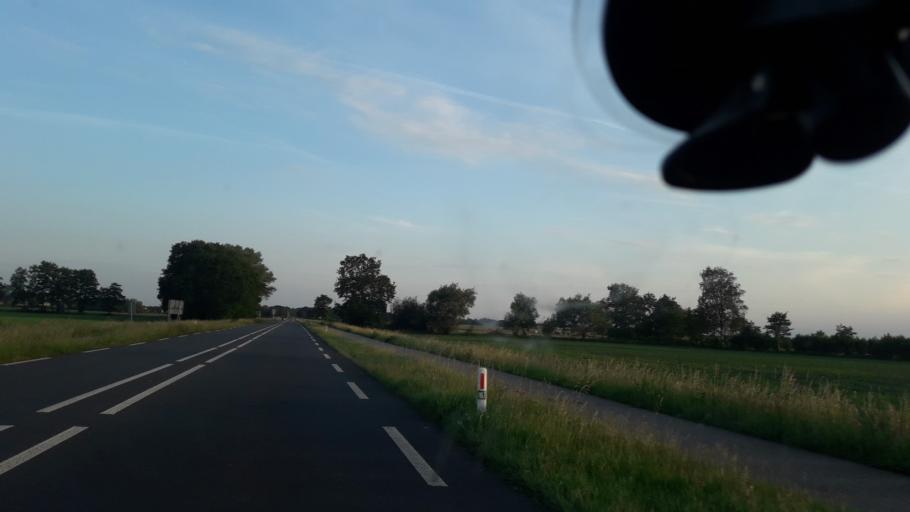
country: NL
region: Gelderland
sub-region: Gemeente Elburg
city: Elburg
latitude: 52.4379
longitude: 5.8304
